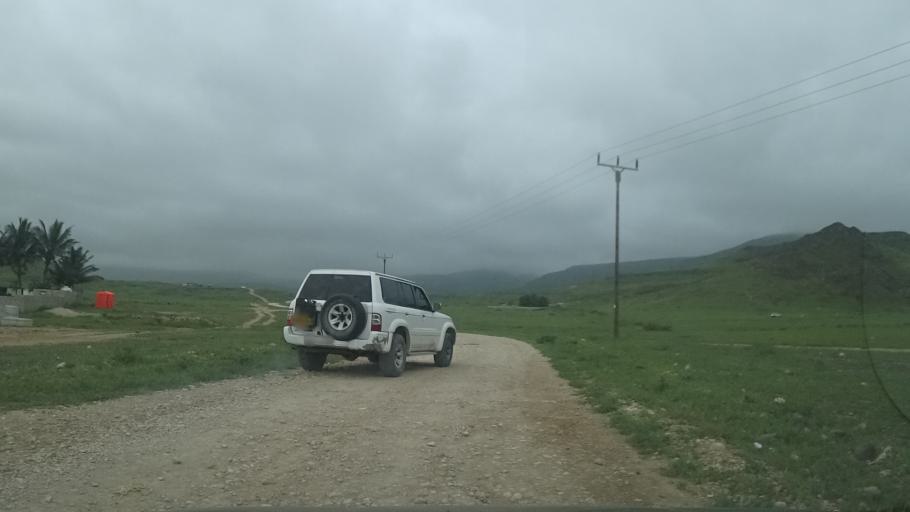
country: OM
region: Zufar
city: Salalah
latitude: 17.1135
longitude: 54.2339
